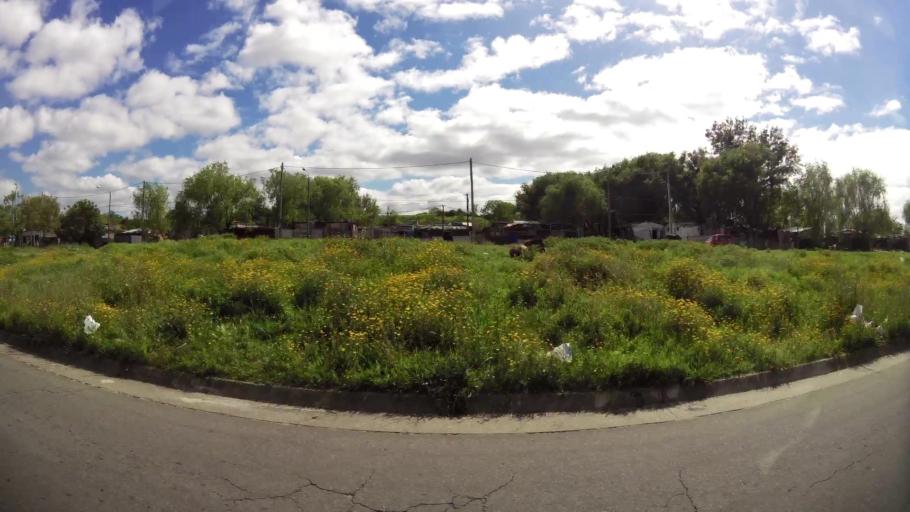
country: UY
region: Montevideo
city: Montevideo
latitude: -34.8811
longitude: -56.1304
